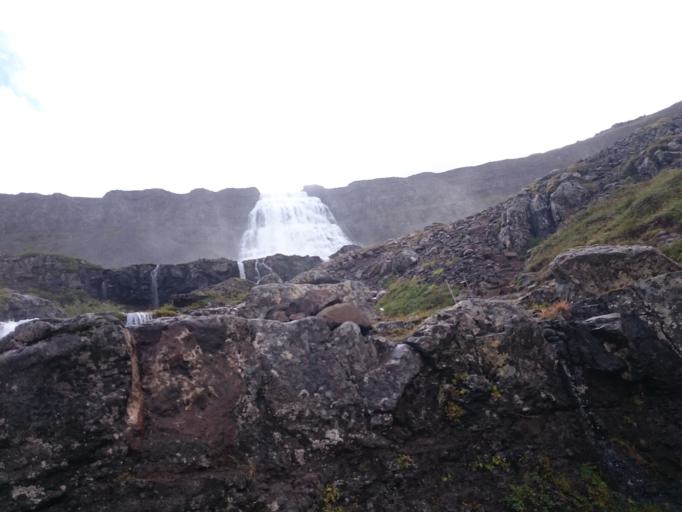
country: IS
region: Westfjords
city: Isafjoerdur
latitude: 65.7350
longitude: -23.2049
